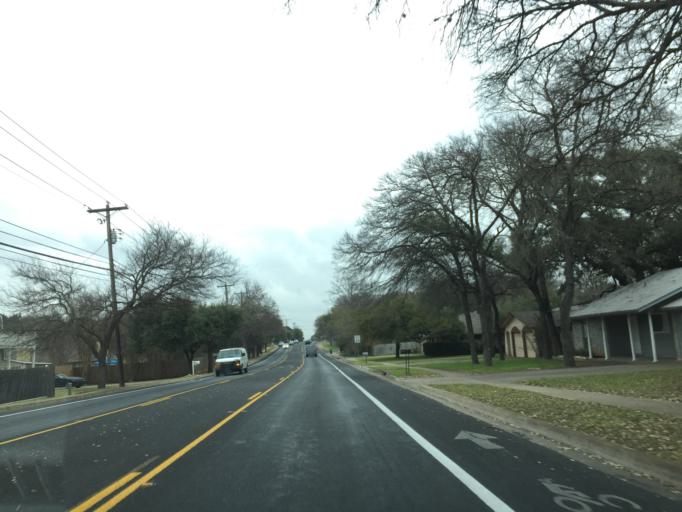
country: US
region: Texas
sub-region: Williamson County
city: Jollyville
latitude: 30.4162
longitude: -97.7394
